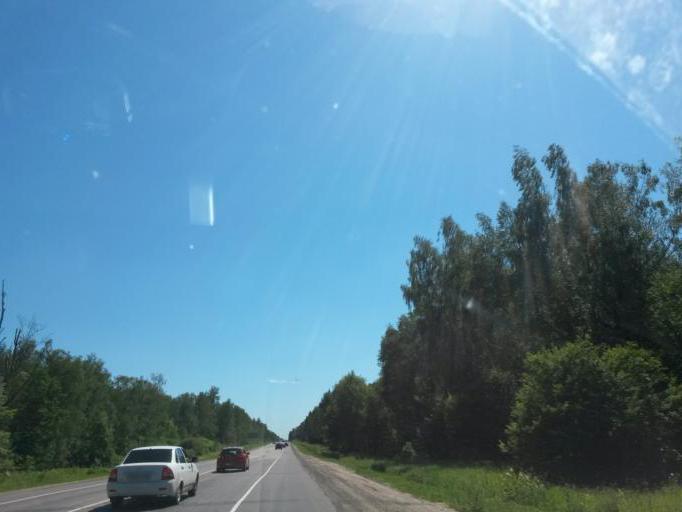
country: RU
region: Moskovskaya
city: Proletarskiy
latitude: 55.0593
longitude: 37.4347
